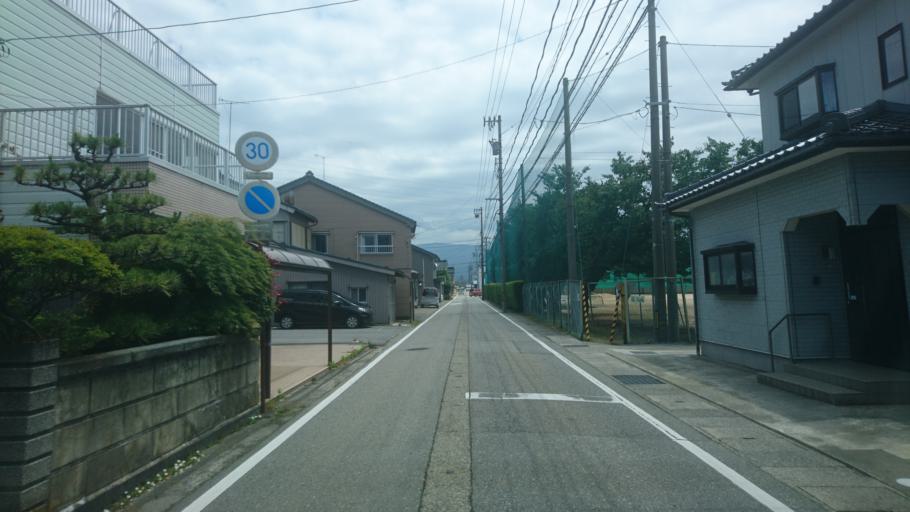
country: JP
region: Toyama
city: Nyuzen
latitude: 36.9396
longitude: 137.5060
